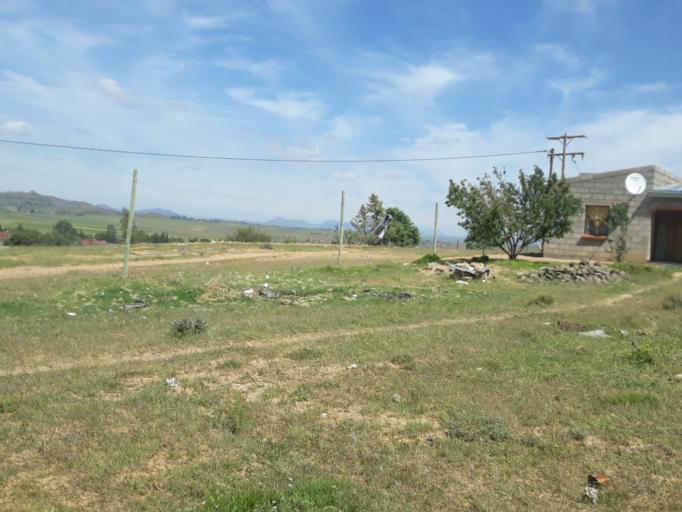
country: LS
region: Mohale's Hoek District
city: Mohale's Hoek
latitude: -30.1028
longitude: 27.4758
